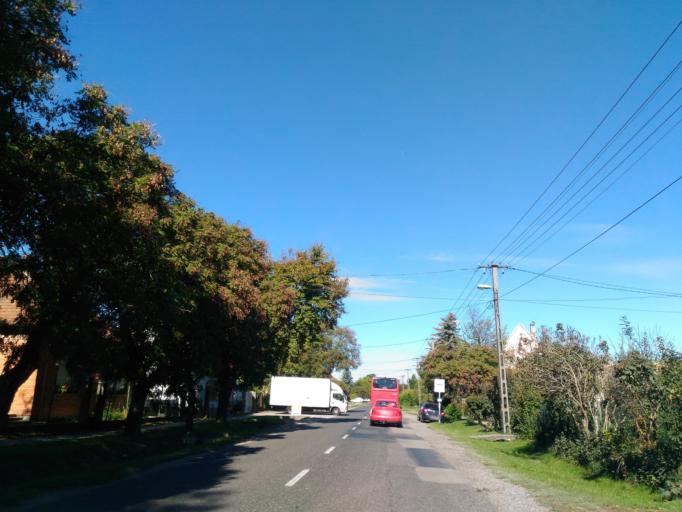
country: HU
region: Fejer
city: Ivancsa
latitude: 47.1448
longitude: 18.8340
